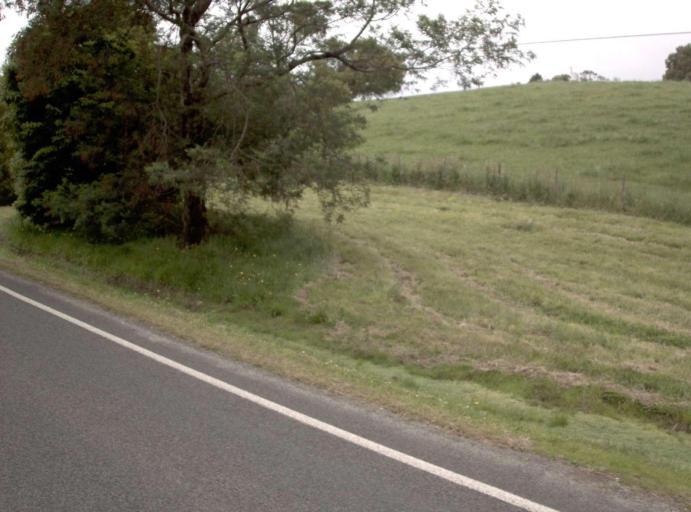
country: AU
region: Victoria
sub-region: Latrobe
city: Moe
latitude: -38.6029
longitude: 146.1302
